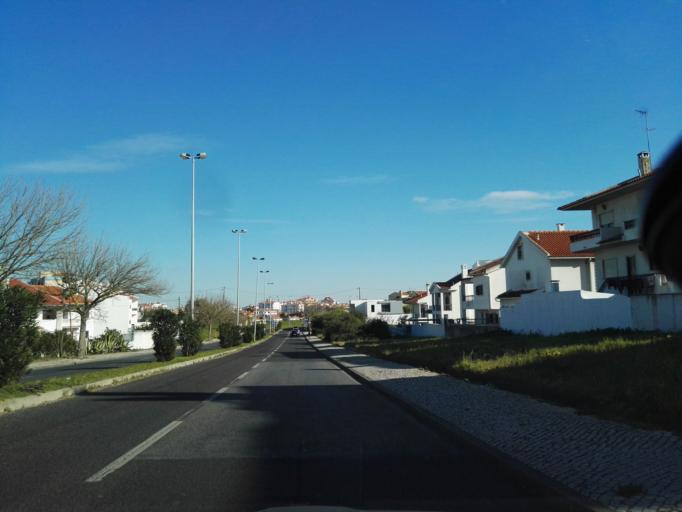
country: PT
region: Setubal
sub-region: Seixal
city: Corroios
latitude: 38.6481
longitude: -9.1626
